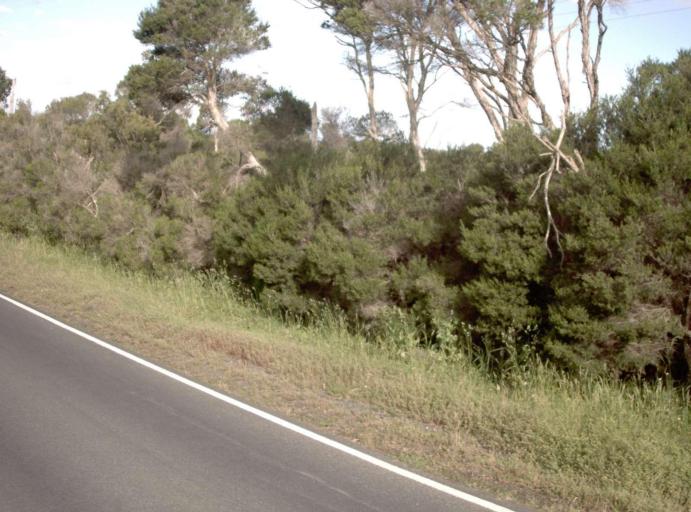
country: AU
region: Victoria
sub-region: Bass Coast
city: North Wonthaggi
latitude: -38.6148
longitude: 145.7451
